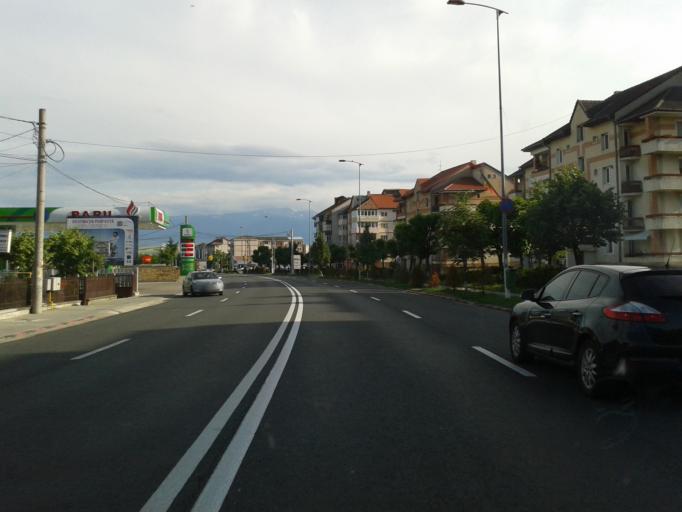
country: RO
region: Hunedoara
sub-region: Oras Hateg
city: Hateg
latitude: 45.6130
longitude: 22.9556
